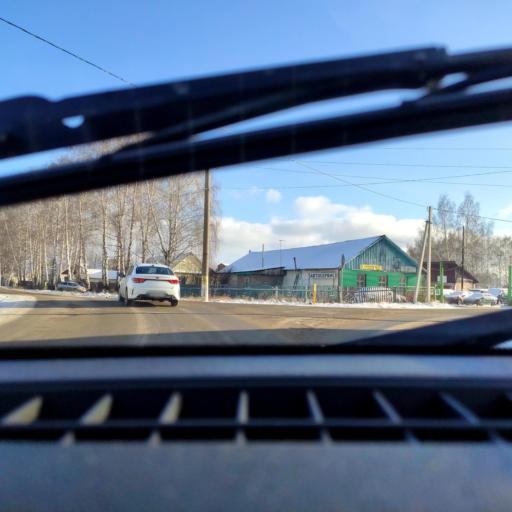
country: RU
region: Bashkortostan
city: Iglino
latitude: 54.8206
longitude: 56.3986
